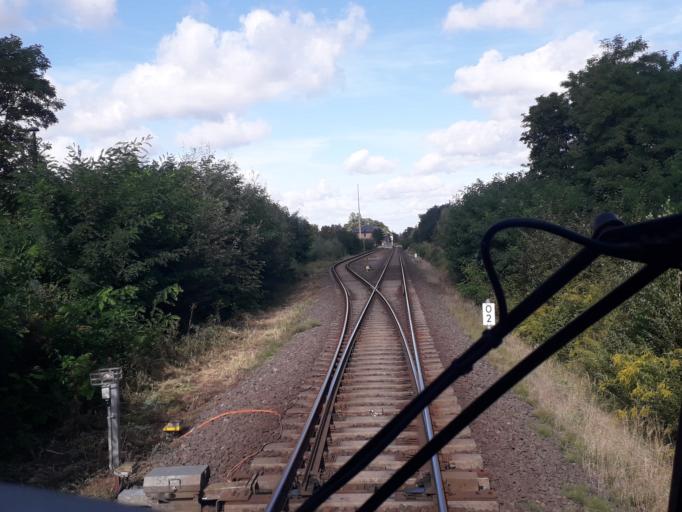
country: DE
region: Brandenburg
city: Kremmen
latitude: 52.7509
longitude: 13.0432
